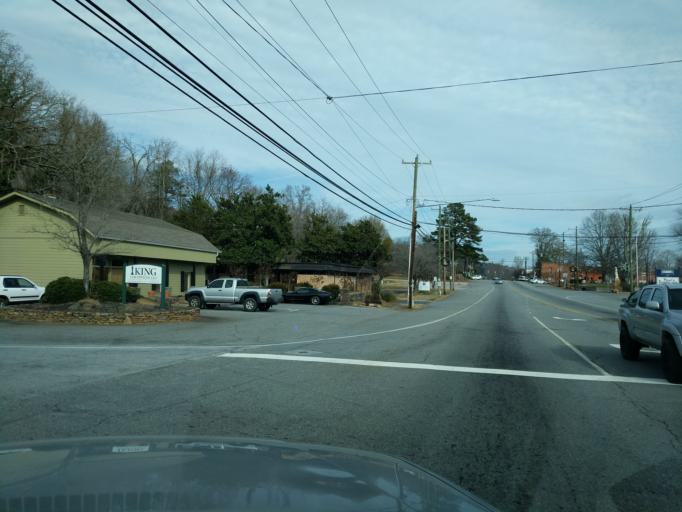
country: US
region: North Carolina
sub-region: Polk County
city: Columbus
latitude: 35.2510
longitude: -82.2000
